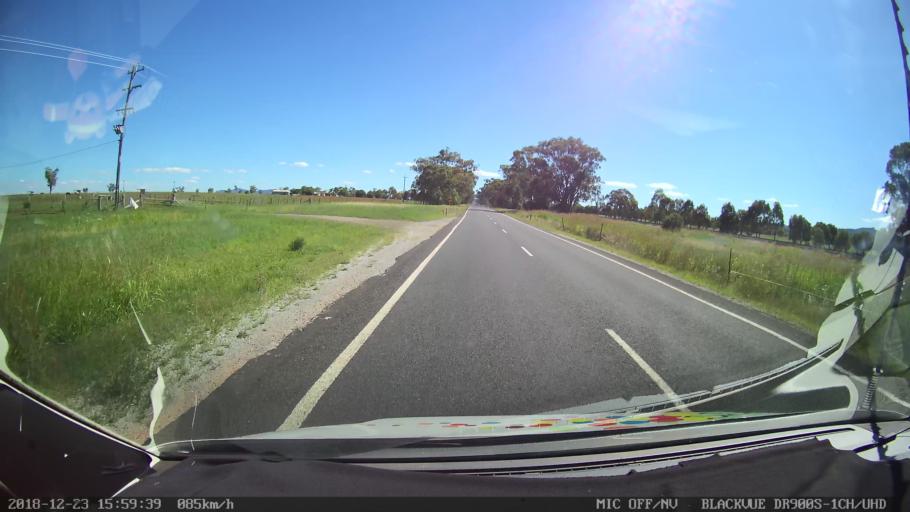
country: AU
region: New South Wales
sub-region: Tamworth Municipality
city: Phillip
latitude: -31.2022
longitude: 150.8314
